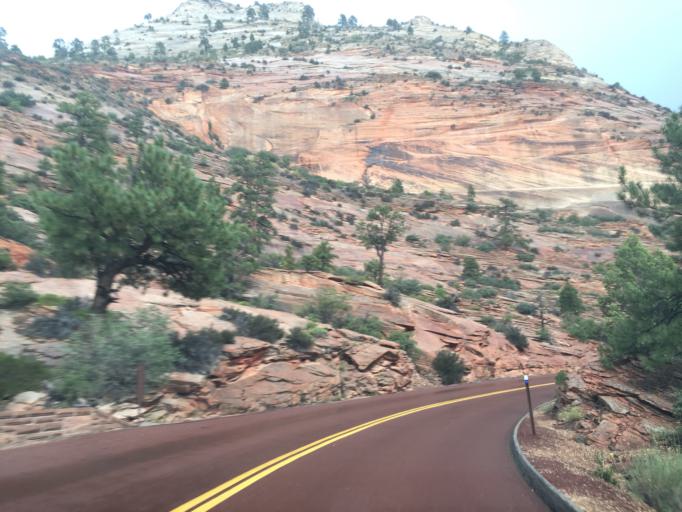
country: US
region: Utah
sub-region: Washington County
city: Hildale
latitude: 37.2254
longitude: -112.9101
